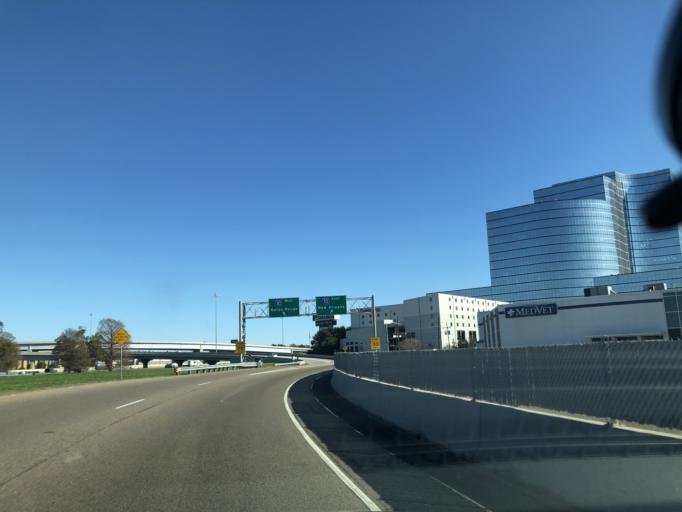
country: US
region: Louisiana
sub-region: Jefferson Parish
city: Metairie
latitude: 29.9949
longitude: -90.1551
